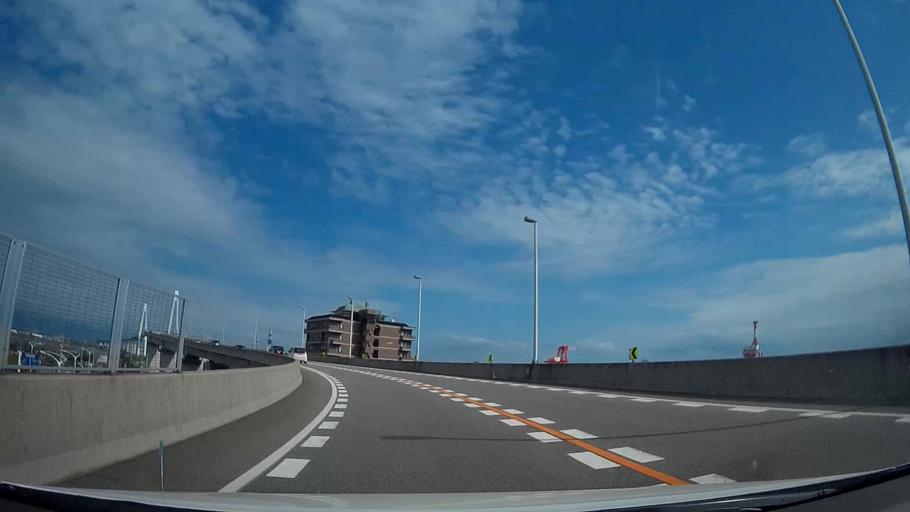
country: JP
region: Toyama
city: Nishishinminato
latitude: 36.7802
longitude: 137.1040
